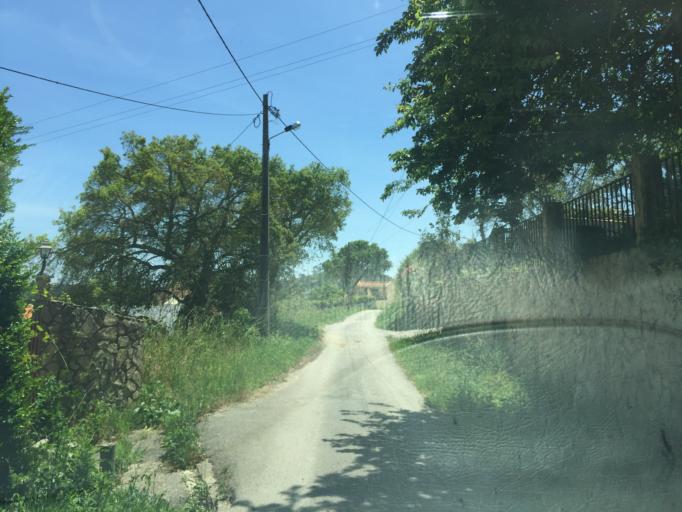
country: PT
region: Lisbon
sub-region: Mafra
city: Venda do Pinheiro
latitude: 38.8963
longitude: -9.2337
